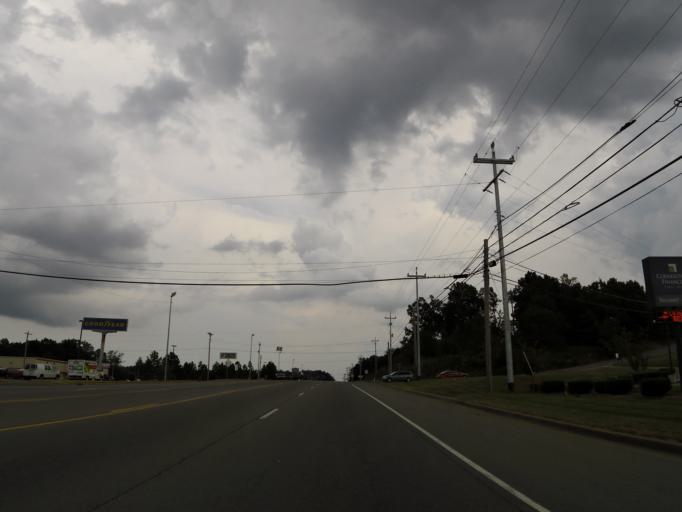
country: US
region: Tennessee
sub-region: Dickson County
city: Dickson
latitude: 36.0538
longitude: -87.3682
